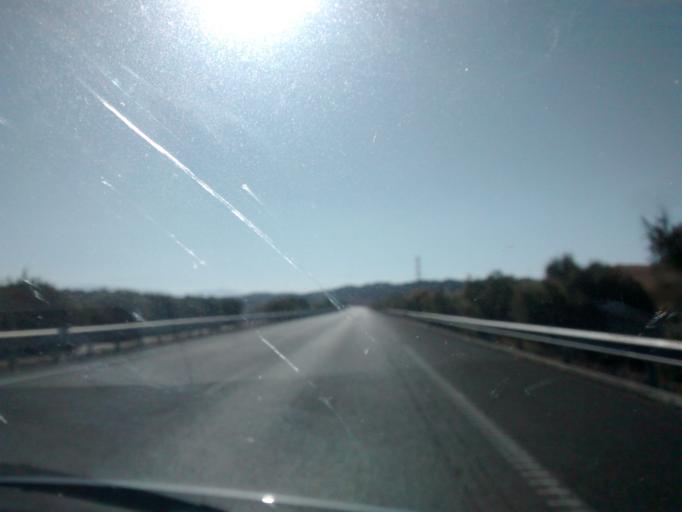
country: ES
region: Andalusia
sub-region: Provincia de Cadiz
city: Paterna de Rivera
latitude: 36.4683
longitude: -5.8399
